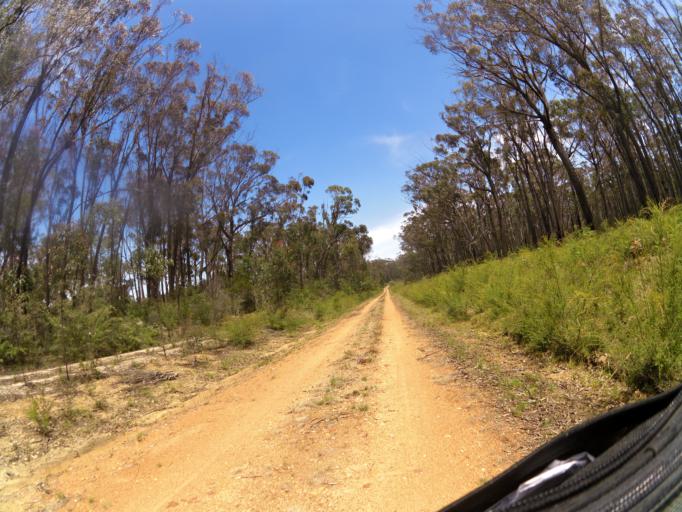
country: AU
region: Victoria
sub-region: East Gippsland
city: Lakes Entrance
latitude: -37.7526
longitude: 147.9724
